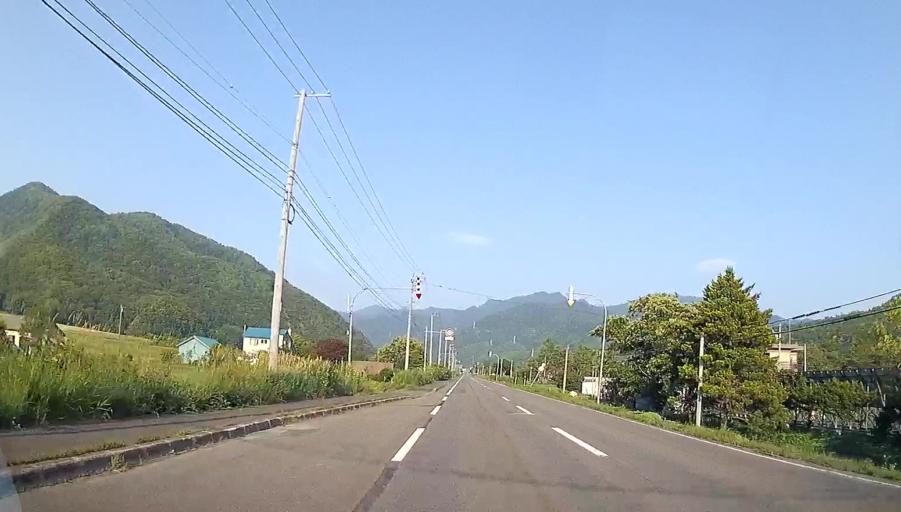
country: JP
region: Hokkaido
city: Shimo-furano
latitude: 42.8932
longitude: 142.5199
